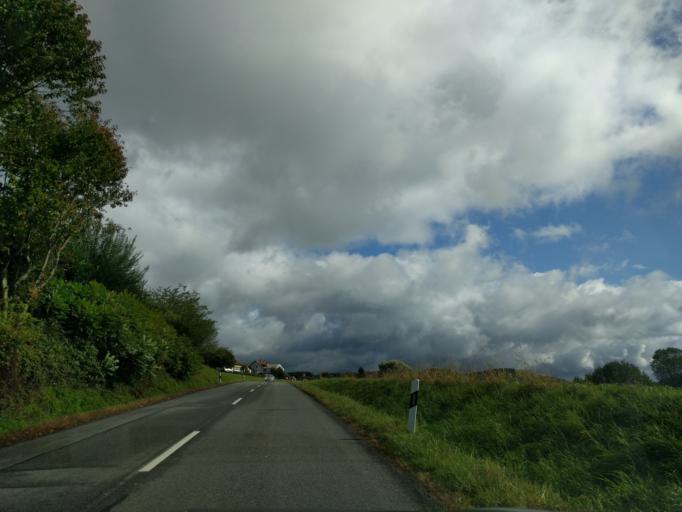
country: DE
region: Bavaria
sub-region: Lower Bavaria
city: Deggendorf
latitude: 48.8335
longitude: 12.9971
